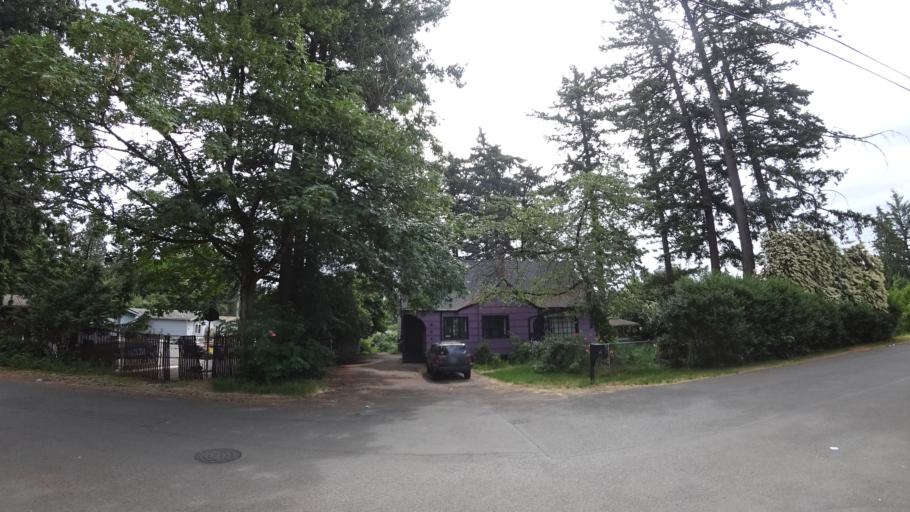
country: US
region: Oregon
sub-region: Multnomah County
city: Lents
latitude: 45.4987
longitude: -122.5286
